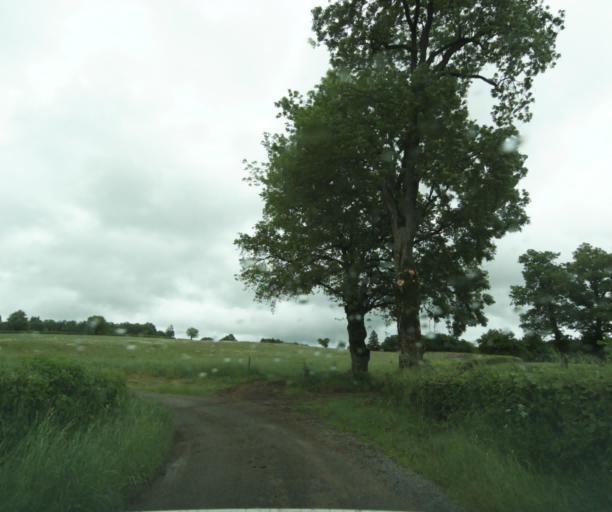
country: FR
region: Bourgogne
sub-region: Departement de Saone-et-Loire
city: Matour
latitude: 46.4391
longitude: 4.4293
